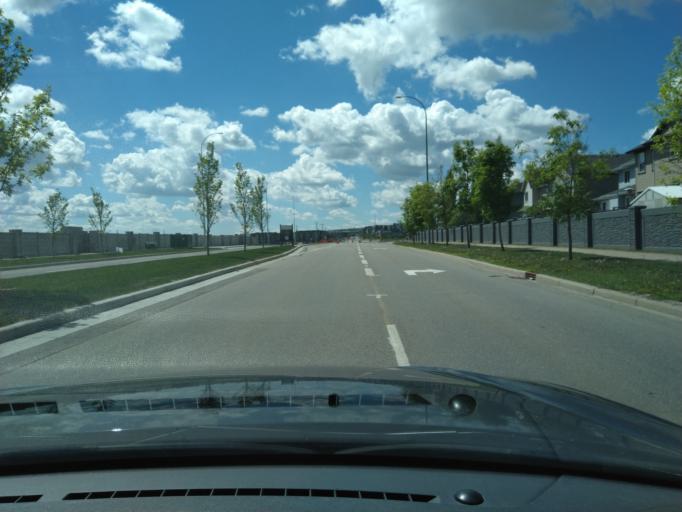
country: CA
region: Alberta
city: Calgary
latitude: 51.1776
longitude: -114.1415
